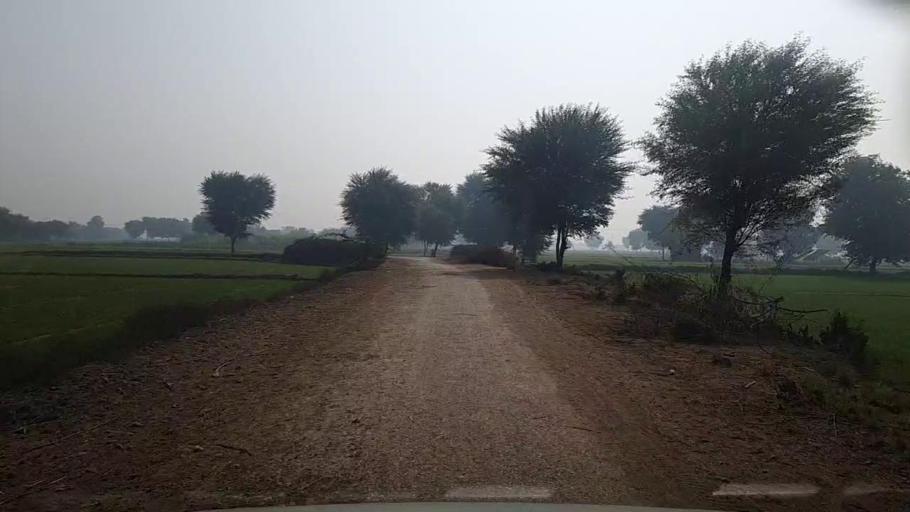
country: PK
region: Sindh
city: Setharja Old
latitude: 27.1505
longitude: 68.4661
